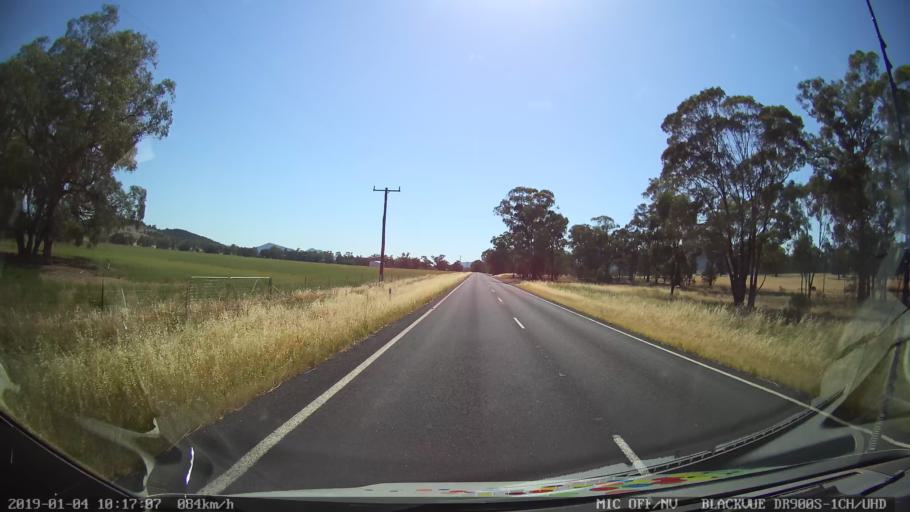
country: AU
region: New South Wales
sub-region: Cabonne
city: Canowindra
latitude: -33.3844
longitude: 148.4468
